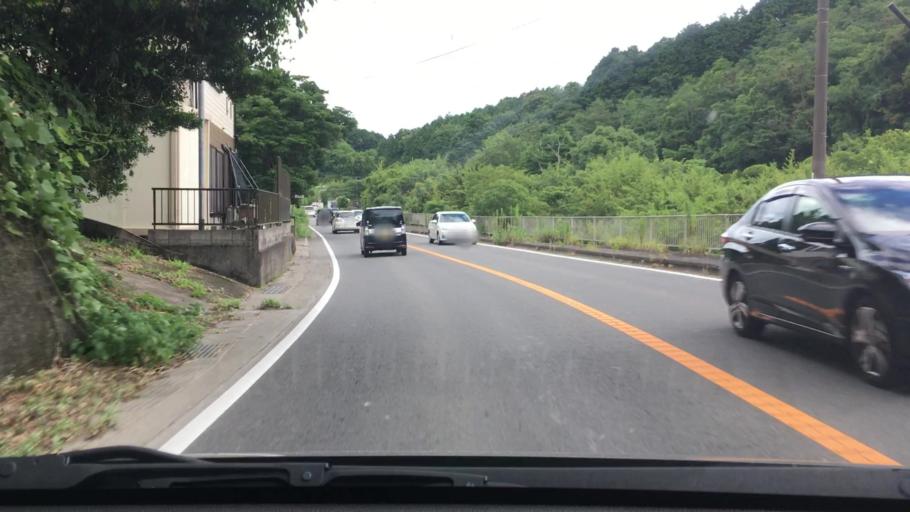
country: JP
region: Nagasaki
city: Togitsu
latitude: 32.9779
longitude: 129.7810
